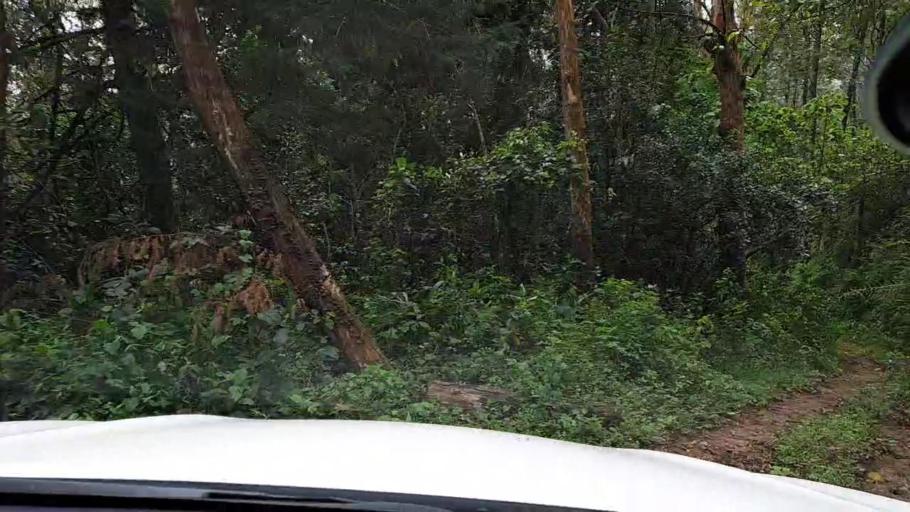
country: RW
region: Western Province
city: Kibuye
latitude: -2.2844
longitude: 29.3048
